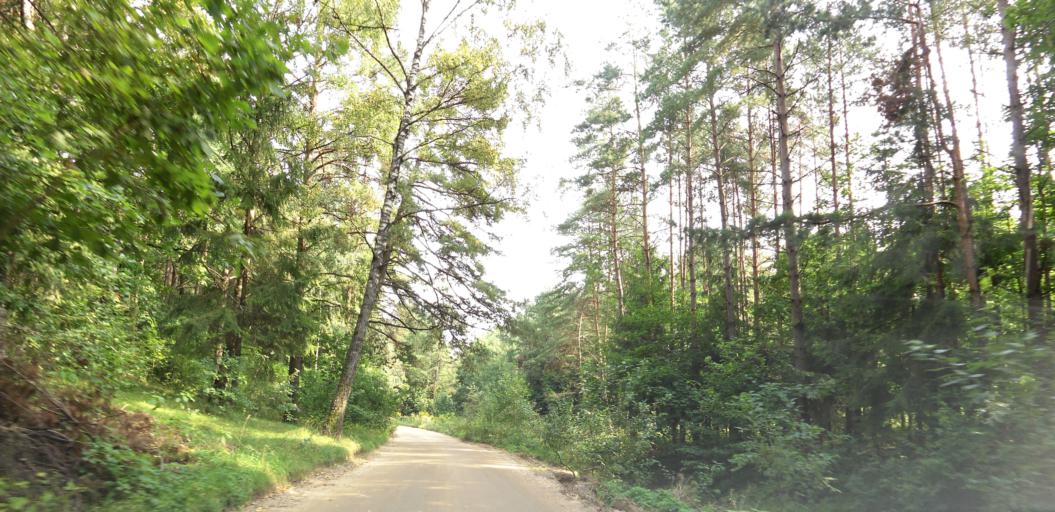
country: LT
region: Vilnius County
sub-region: Vilnius
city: Fabijoniskes
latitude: 54.7497
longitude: 25.2376
